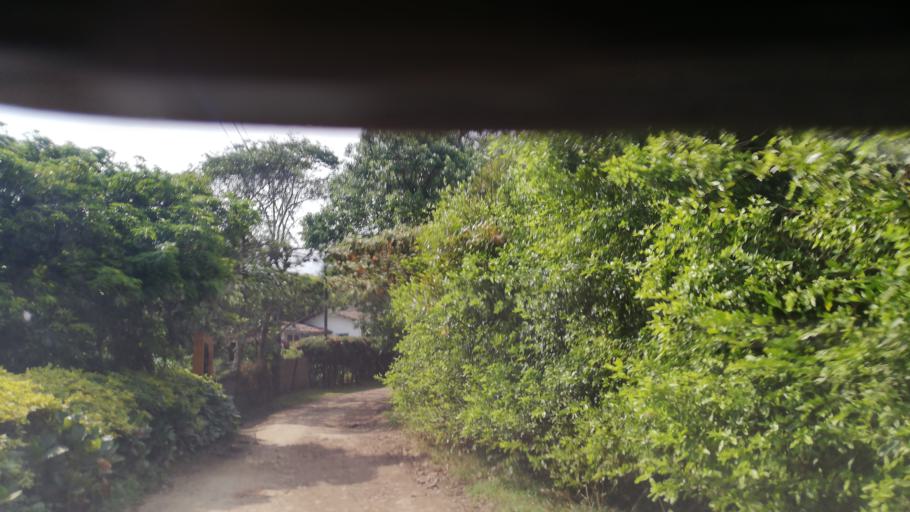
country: CO
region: Valle del Cauca
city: Cali
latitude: 3.4965
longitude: -76.5462
